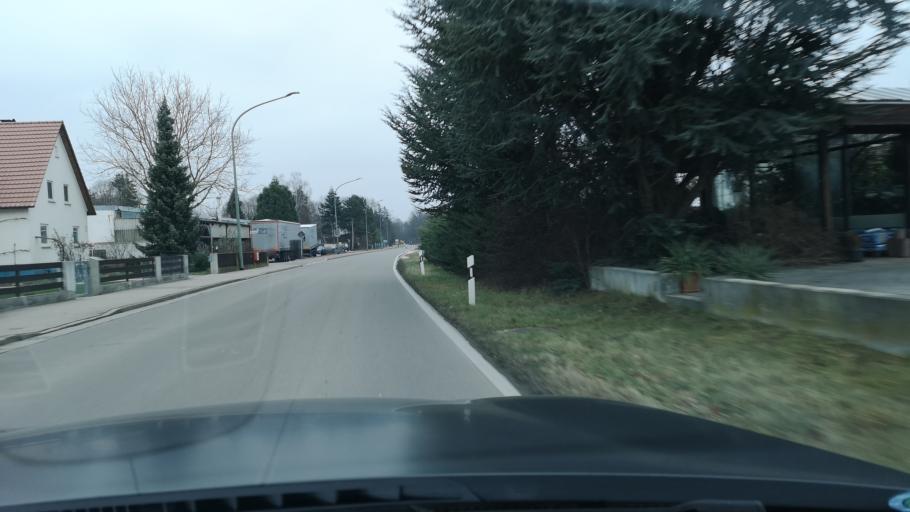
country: DE
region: Bavaria
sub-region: Swabia
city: Leipheim
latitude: 48.4303
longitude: 10.1898
